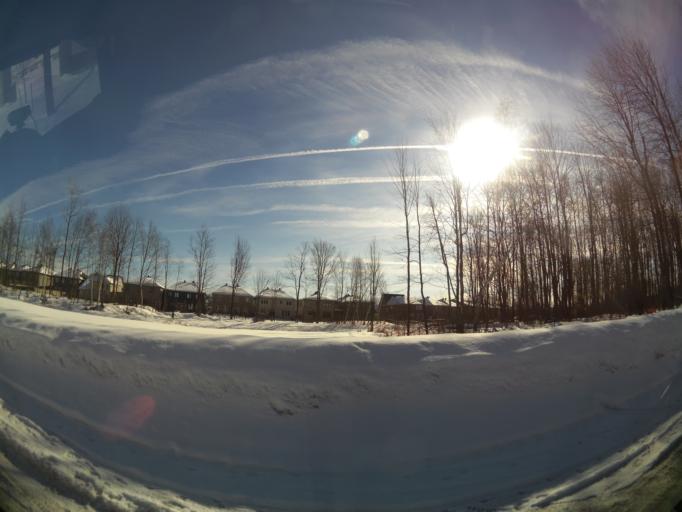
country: CA
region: Ontario
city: Ottawa
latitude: 45.4364
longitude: -75.5084
